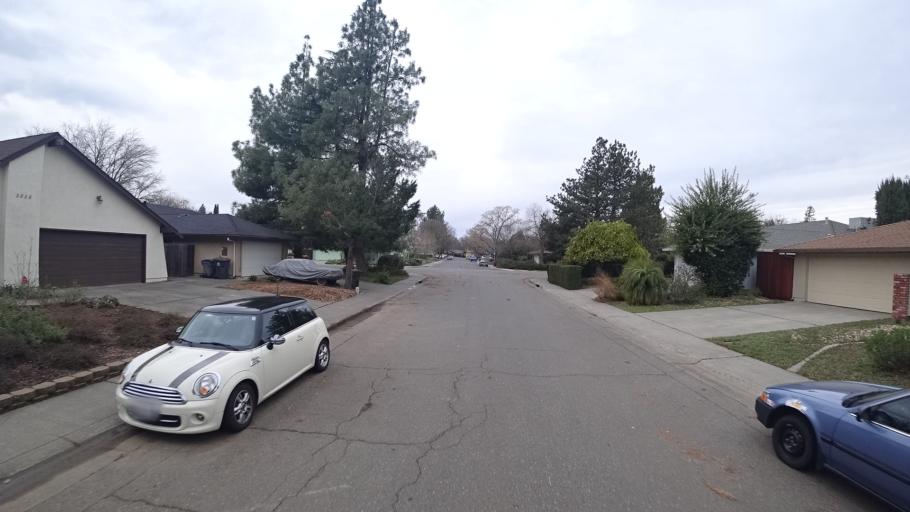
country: US
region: California
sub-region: Yolo County
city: Davis
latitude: 38.5590
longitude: -121.7169
